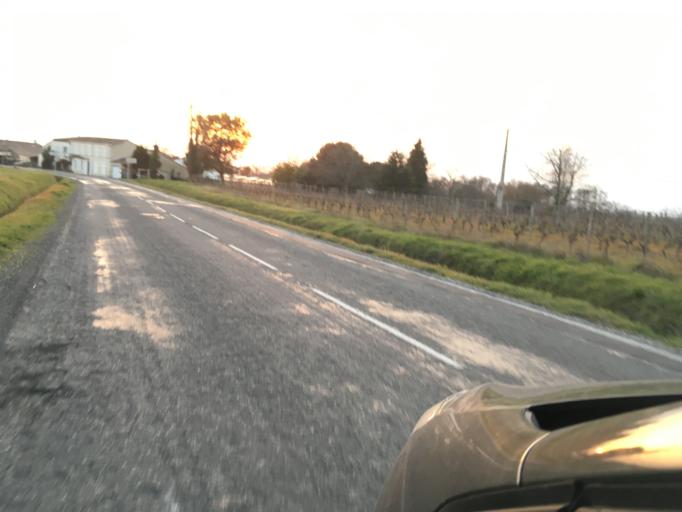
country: FR
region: Aquitaine
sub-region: Departement de la Gironde
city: Saint-Ciers-sur-Gironde
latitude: 45.2992
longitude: -0.6039
